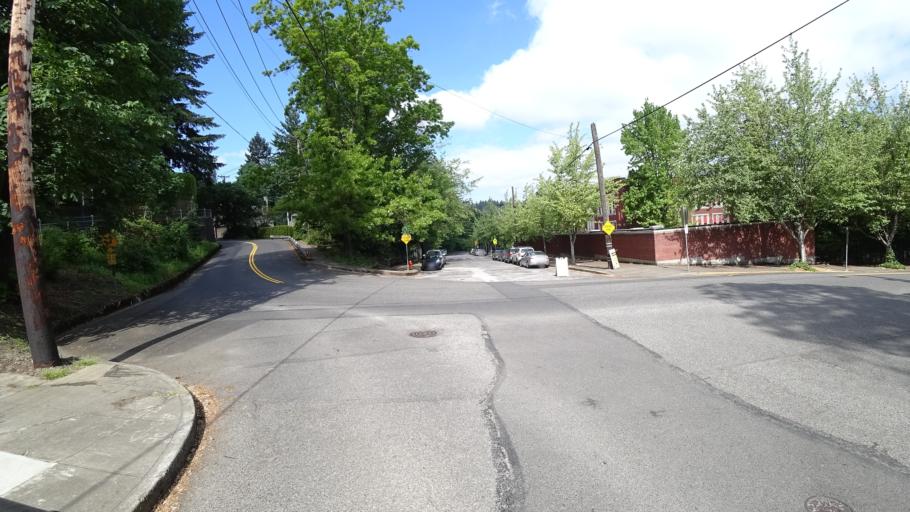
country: US
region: Oregon
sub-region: Multnomah County
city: Portland
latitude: 45.5093
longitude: -122.6990
